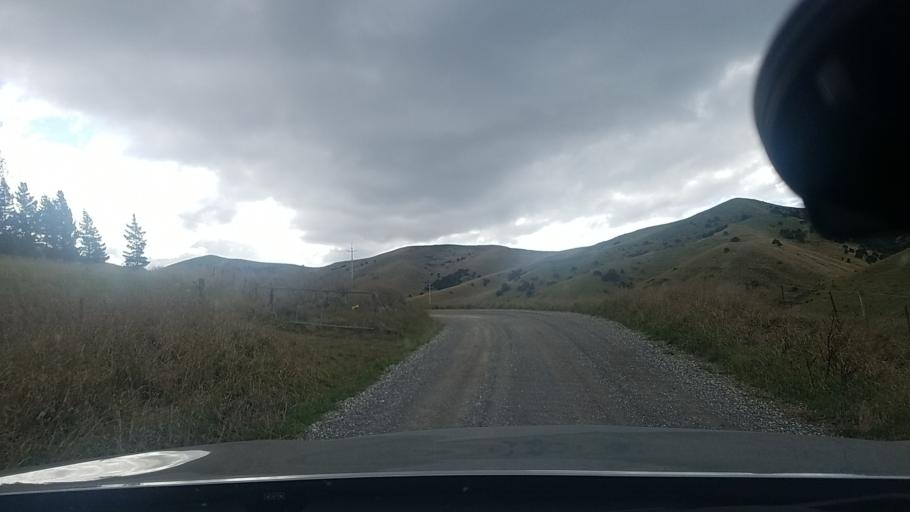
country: NZ
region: Marlborough
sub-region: Marlborough District
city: Blenheim
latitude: -41.5889
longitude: 174.0920
